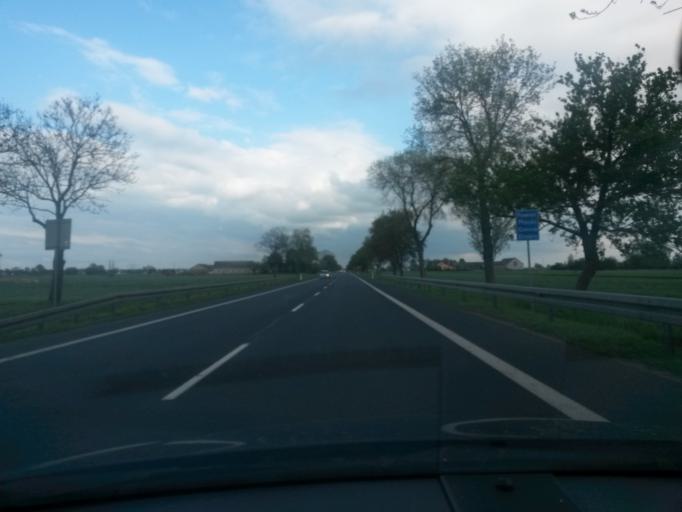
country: PL
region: Masovian Voivodeship
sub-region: Powiat plocki
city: Drobin
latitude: 52.7638
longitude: 19.9437
